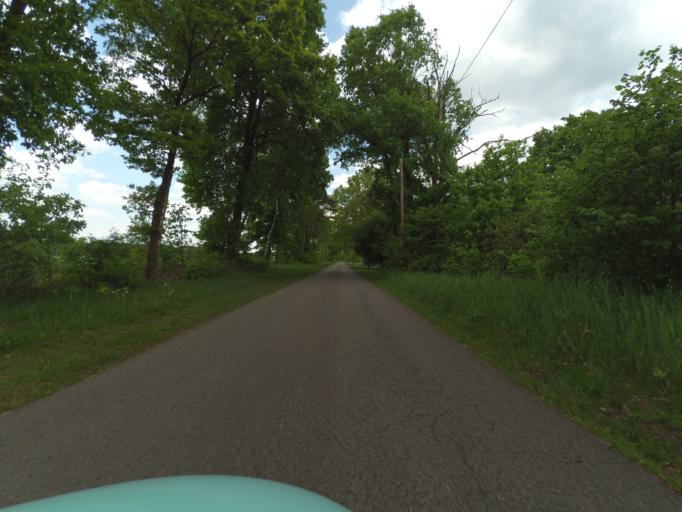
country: DE
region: Lower Saxony
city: Wietze
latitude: 52.5727
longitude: 9.8353
